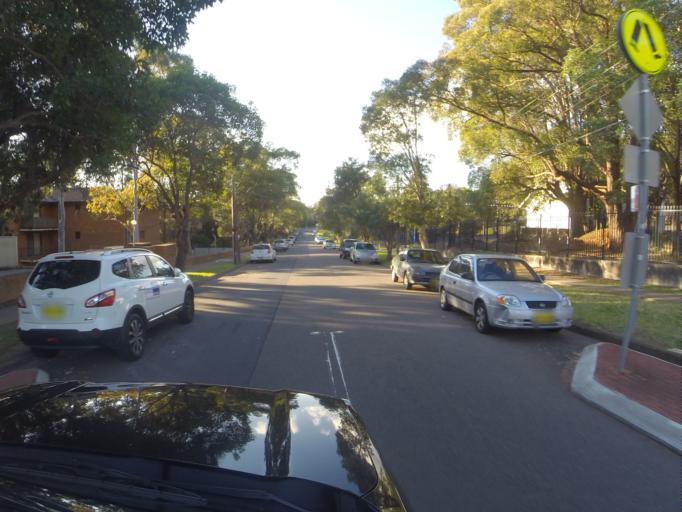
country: AU
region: New South Wales
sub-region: Canterbury
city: Canterbury
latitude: -33.9083
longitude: 151.1216
